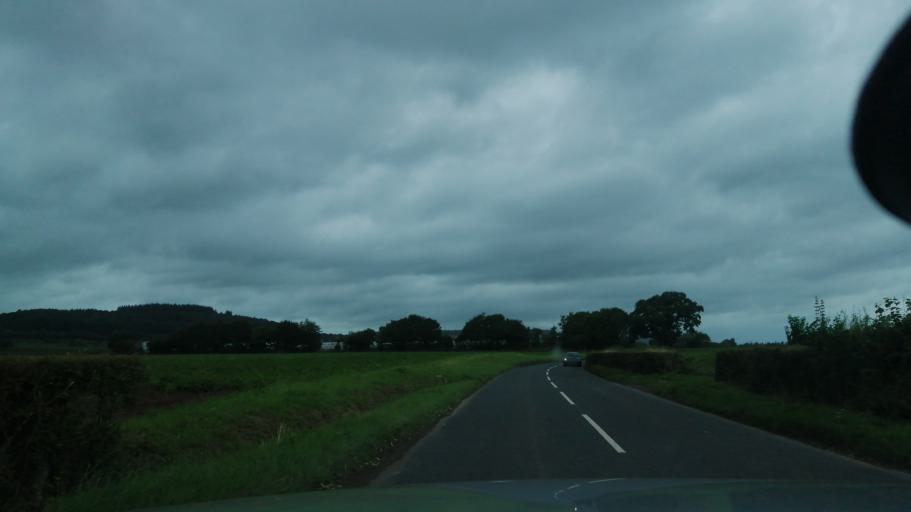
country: GB
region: England
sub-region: Herefordshire
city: Kingstone
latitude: 52.0175
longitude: -2.8476
